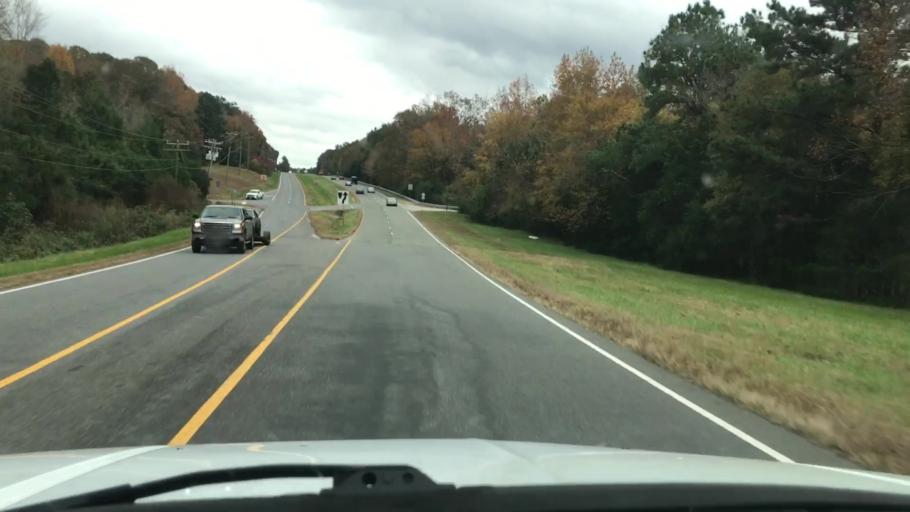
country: US
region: Virginia
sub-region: Henrico County
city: Short Pump
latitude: 37.6076
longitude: -77.7282
